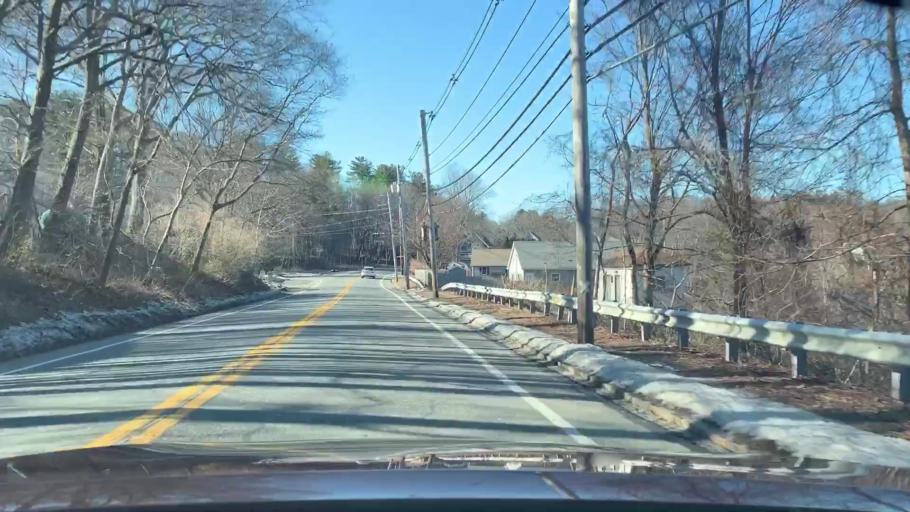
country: US
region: Massachusetts
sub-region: Essex County
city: Gloucester
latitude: 42.6138
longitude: -70.6929
